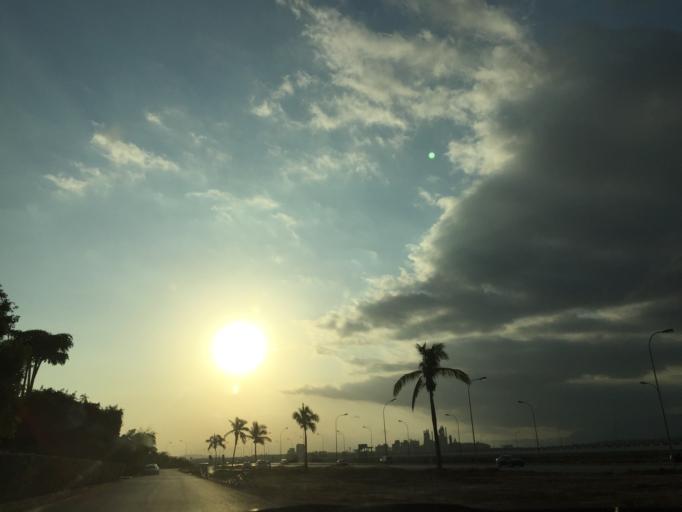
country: OM
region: Zufar
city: Salalah
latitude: 16.9828
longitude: 54.0152
